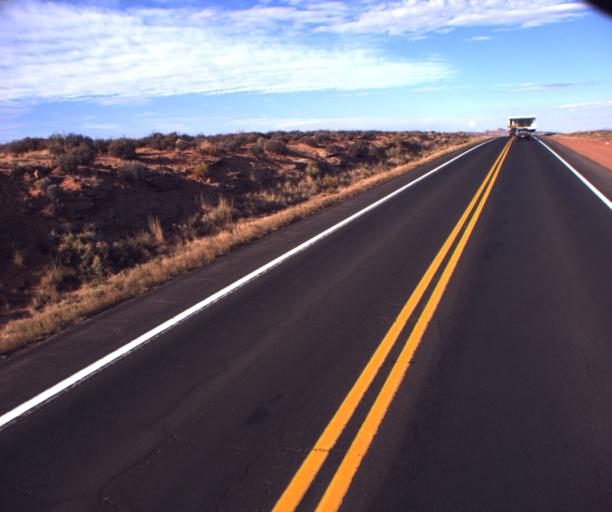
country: US
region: Arizona
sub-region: Apache County
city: Lukachukai
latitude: 36.9630
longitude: -109.4481
